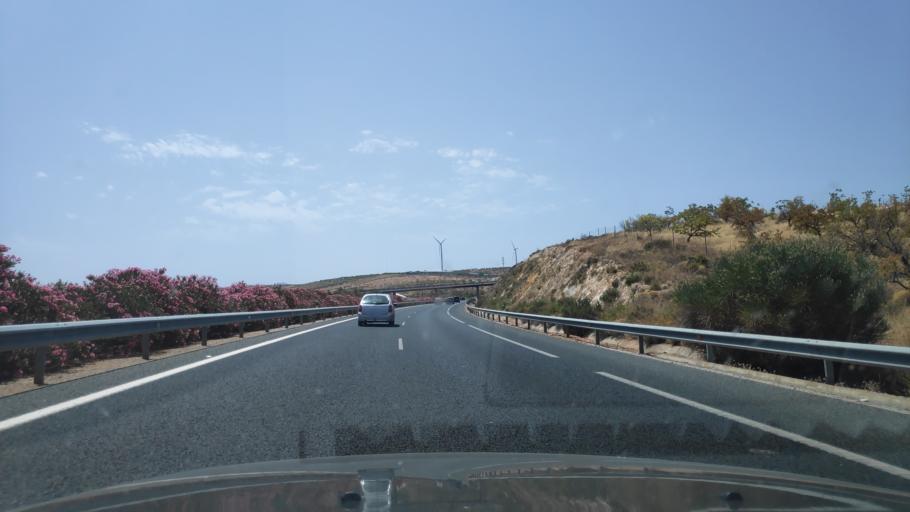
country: ES
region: Andalusia
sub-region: Provincia de Granada
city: Padul
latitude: 37.0157
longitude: -3.6402
